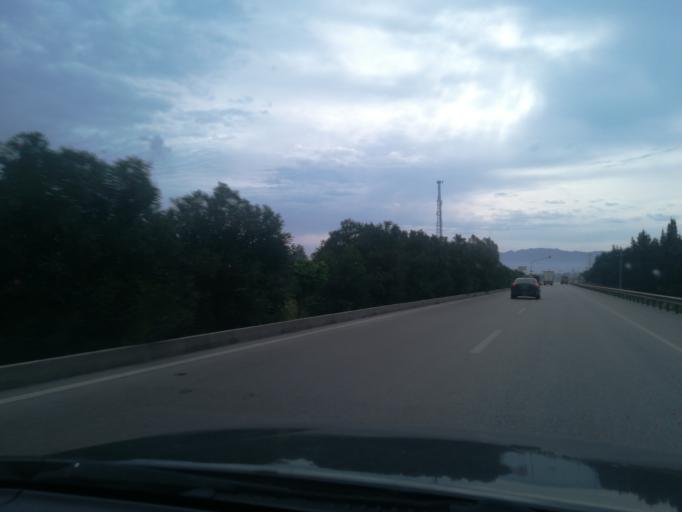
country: TR
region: Adana
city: Yakapinar
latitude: 36.9657
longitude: 35.6057
